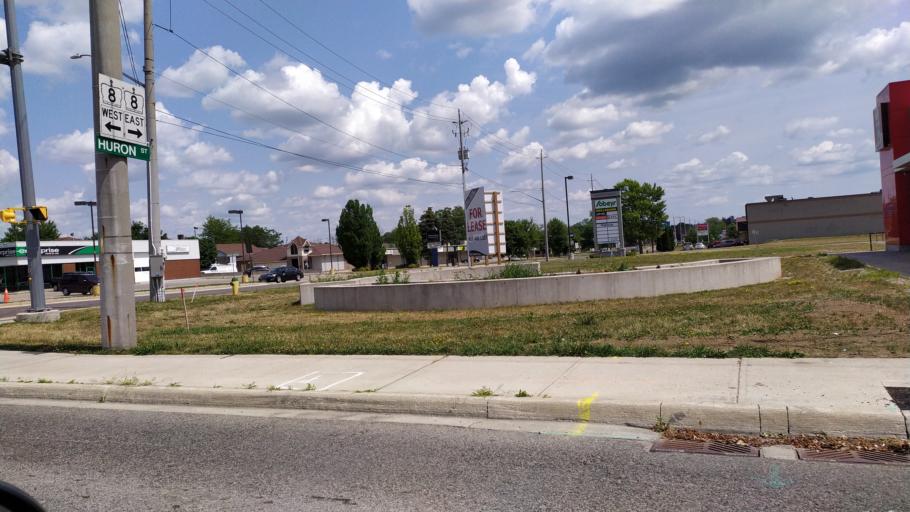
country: CA
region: Ontario
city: Stratford
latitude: 43.3809
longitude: -81.0042
